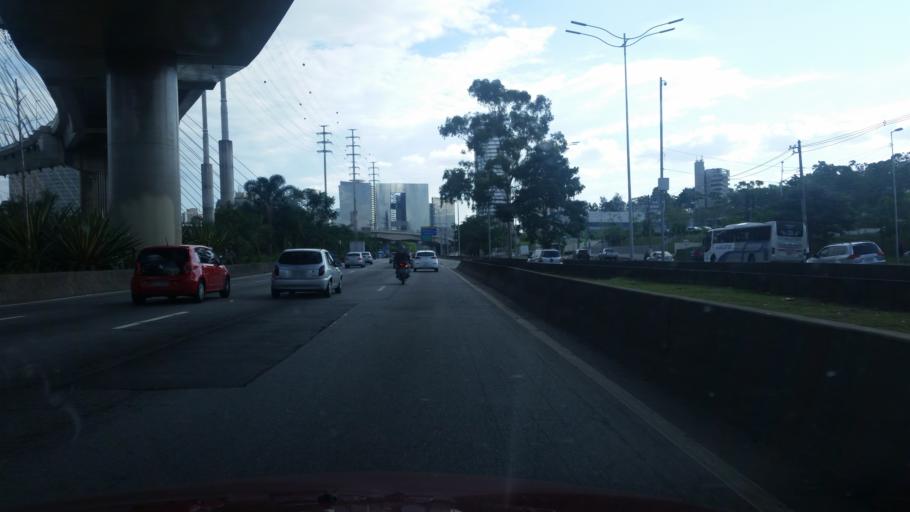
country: BR
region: Sao Paulo
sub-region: Sao Paulo
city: Sao Paulo
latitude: -23.6106
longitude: -46.7001
